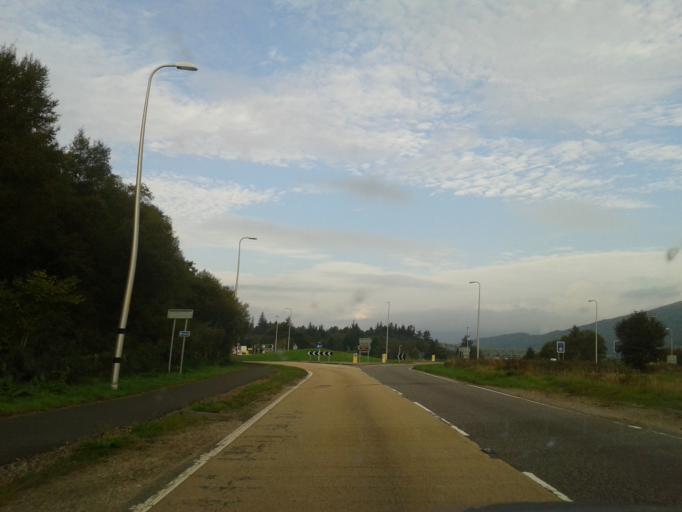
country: GB
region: Scotland
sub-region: Highland
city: Fort William
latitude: 56.6843
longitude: -5.1728
